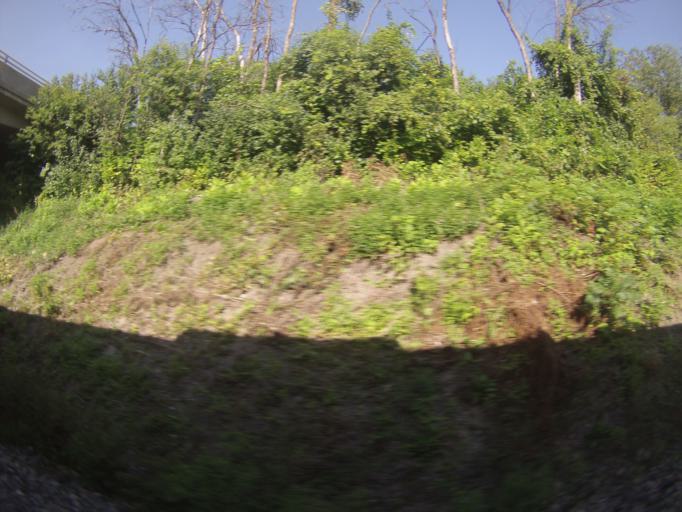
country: CA
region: Ontario
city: Ottawa
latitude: 45.3794
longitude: -75.6911
